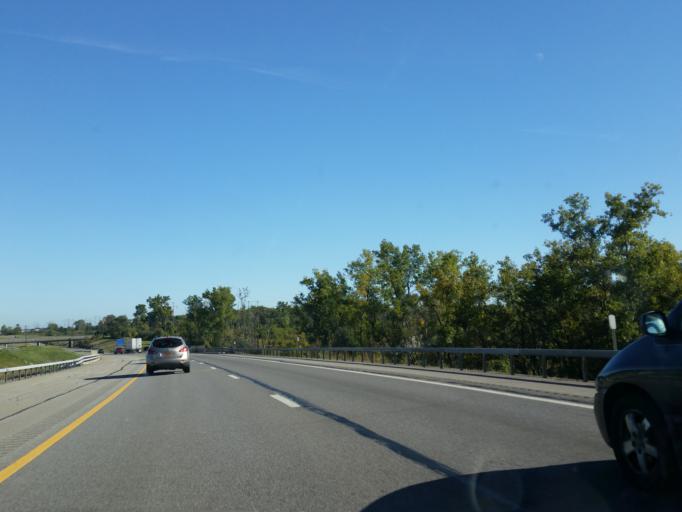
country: US
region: New York
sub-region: Erie County
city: Blasdell
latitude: 42.7658
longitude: -78.8183
